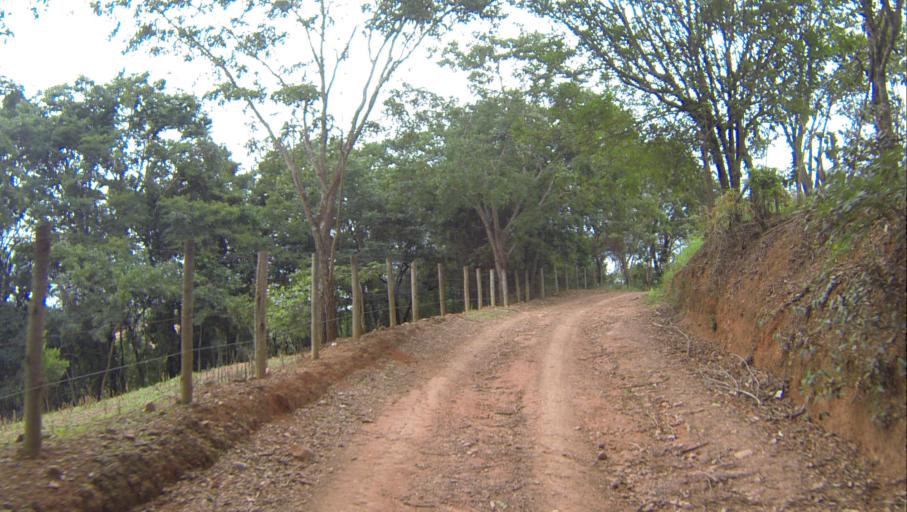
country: BR
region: Minas Gerais
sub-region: Brumadinho
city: Brumadinho
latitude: -20.1571
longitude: -44.1274
